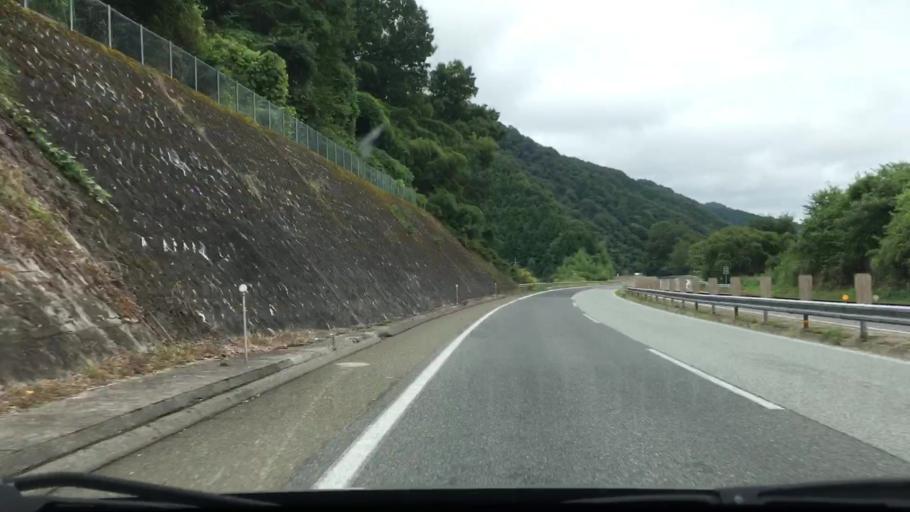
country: JP
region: Hiroshima
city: Shobara
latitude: 34.8375
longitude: 133.0821
